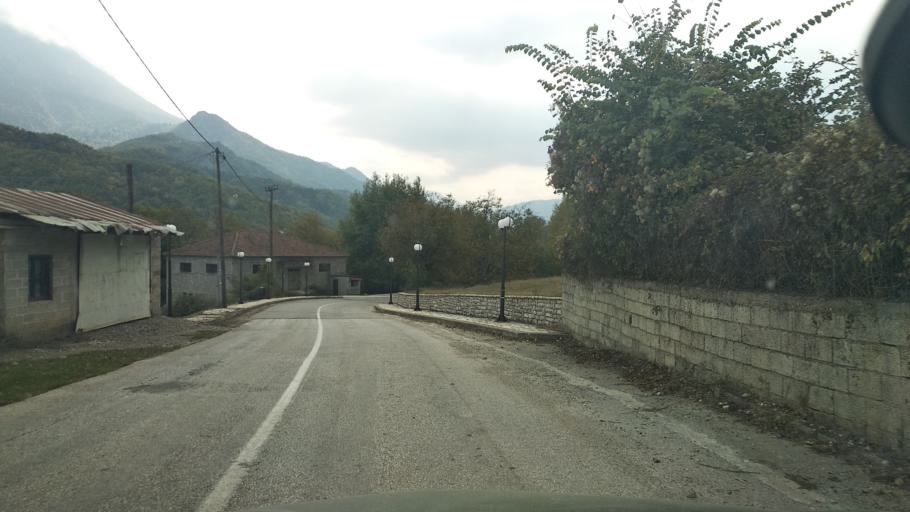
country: GR
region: Thessaly
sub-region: Trikala
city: Kastraki
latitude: 39.6918
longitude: 21.5186
